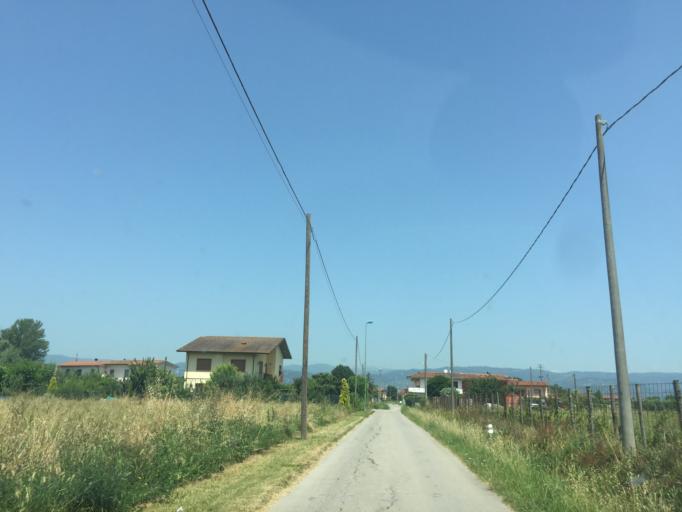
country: IT
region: Tuscany
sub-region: Provincia di Pistoia
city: Anchione
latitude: 43.8245
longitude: 10.7648
